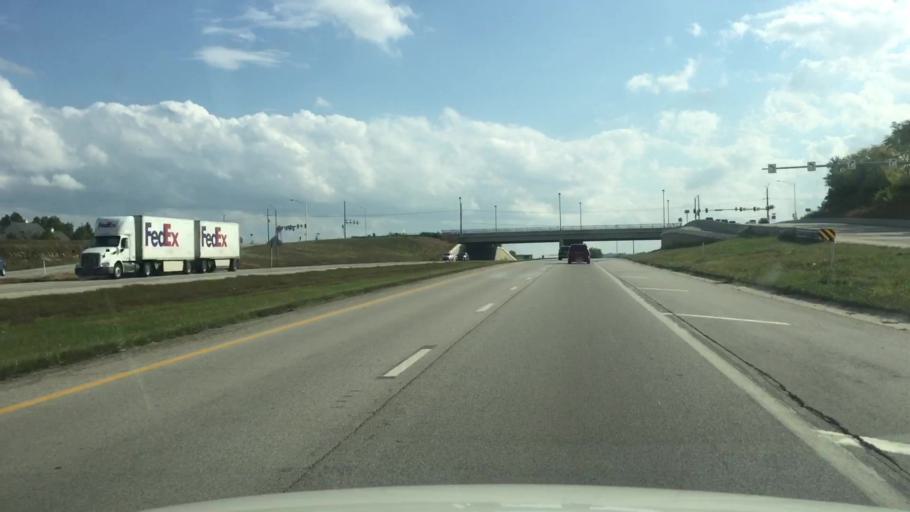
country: US
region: Kansas
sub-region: Johnson County
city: Lenexa
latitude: 38.8423
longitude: -94.6766
